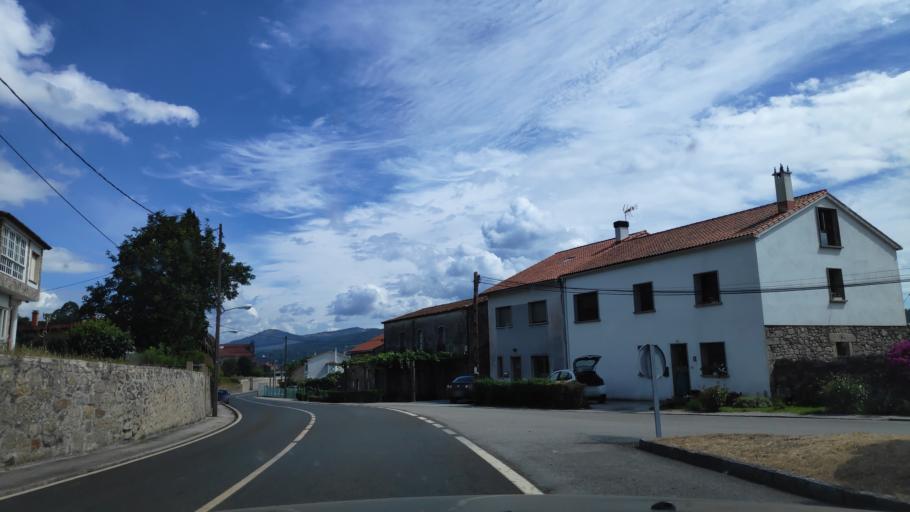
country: ES
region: Galicia
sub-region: Provincia da Coruna
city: Padron
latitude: 42.7344
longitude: -8.6659
